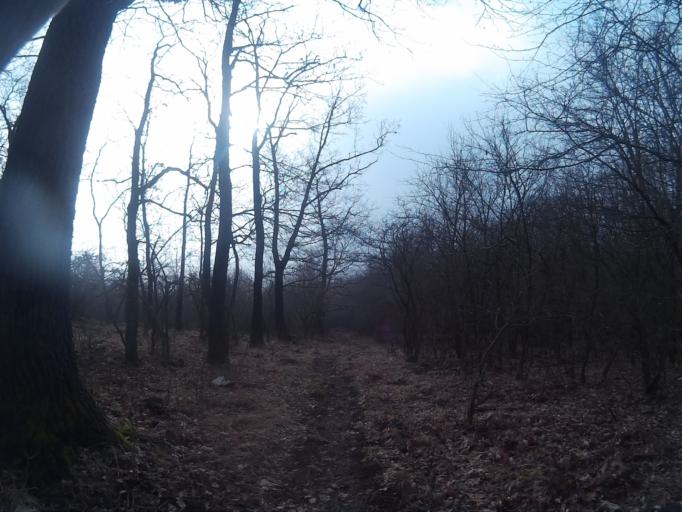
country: HU
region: Komarom-Esztergom
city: Tarjan
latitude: 47.6350
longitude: 18.4781
